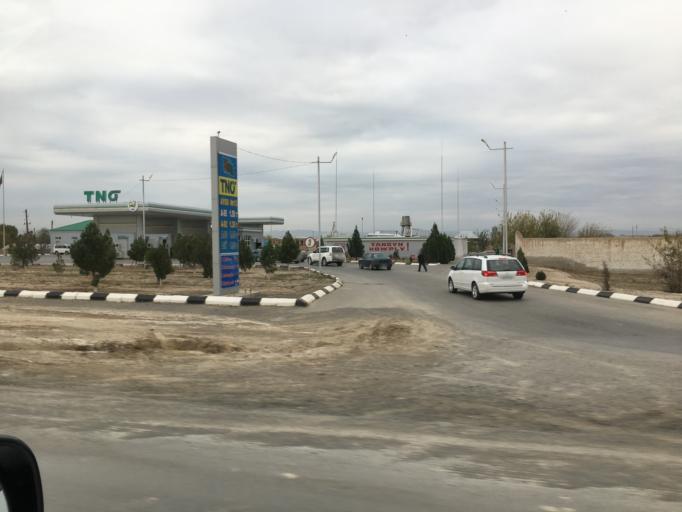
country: TM
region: Ahal
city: Kaka
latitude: 37.3607
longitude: 59.6306
